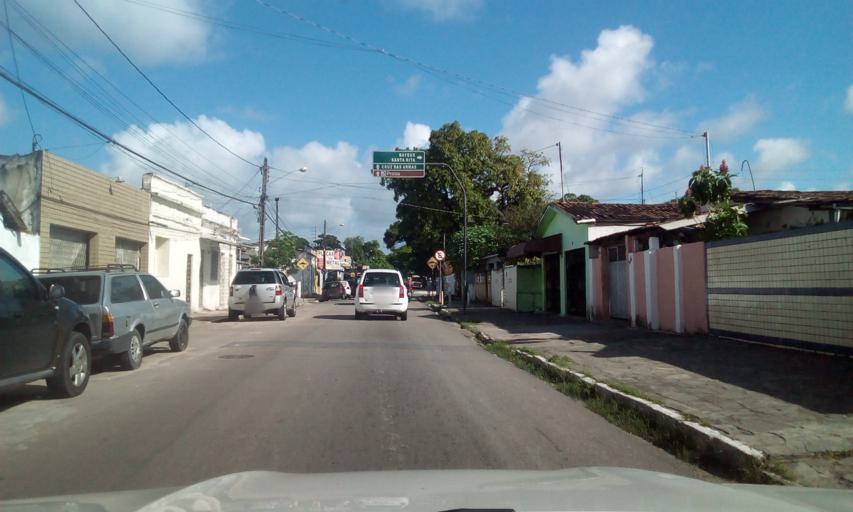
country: BR
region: Paraiba
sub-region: Joao Pessoa
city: Joao Pessoa
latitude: -7.1223
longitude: -34.8904
